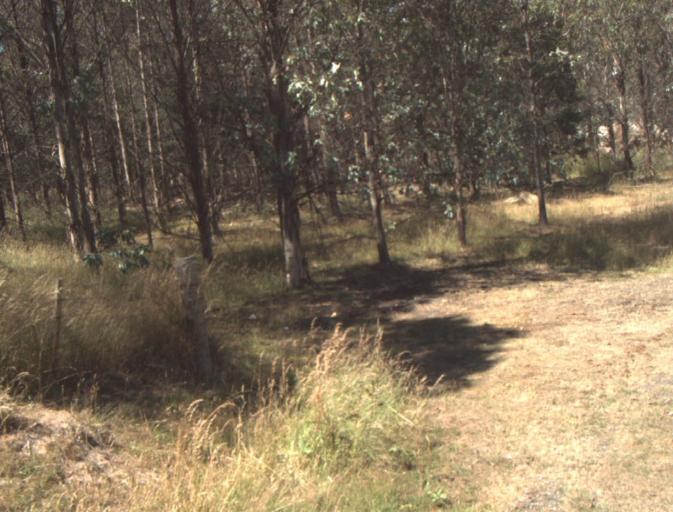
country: AU
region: Tasmania
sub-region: Dorset
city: Scottsdale
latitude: -41.2696
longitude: 147.3521
